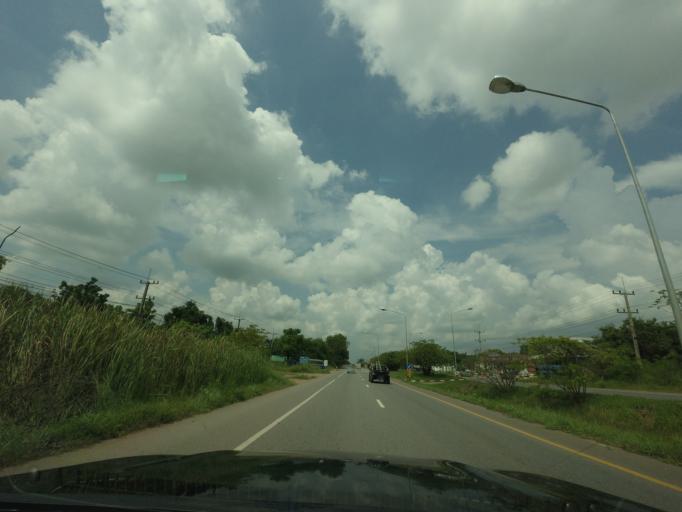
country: TH
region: Khon Kaen
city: Nong Ruea
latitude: 16.4893
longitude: 102.4530
